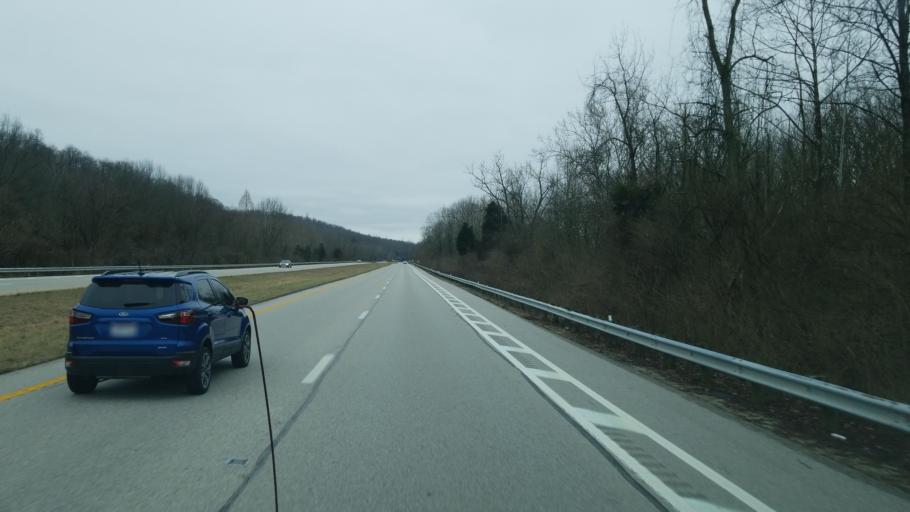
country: US
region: Ohio
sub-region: Clermont County
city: Withamsville
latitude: 39.0166
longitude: -84.3099
